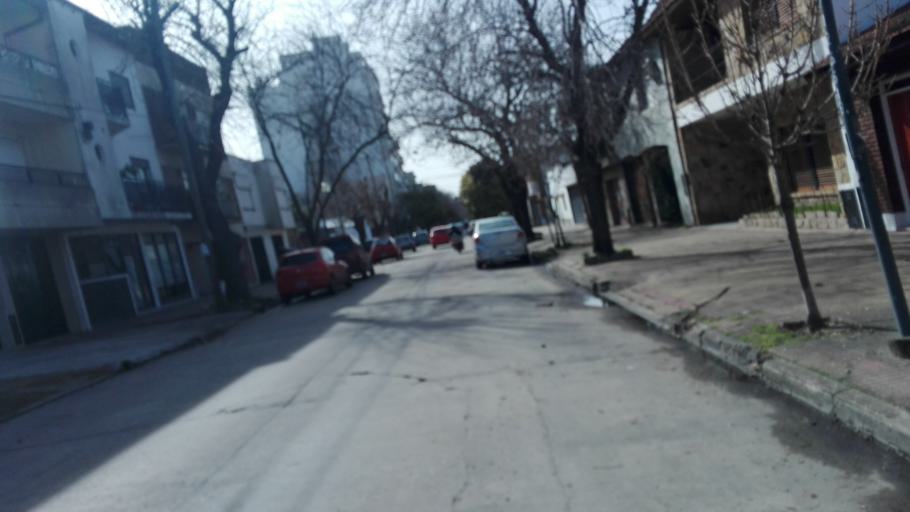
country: AR
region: Buenos Aires
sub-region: Partido de La Plata
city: La Plata
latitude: -34.9112
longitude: -57.9724
